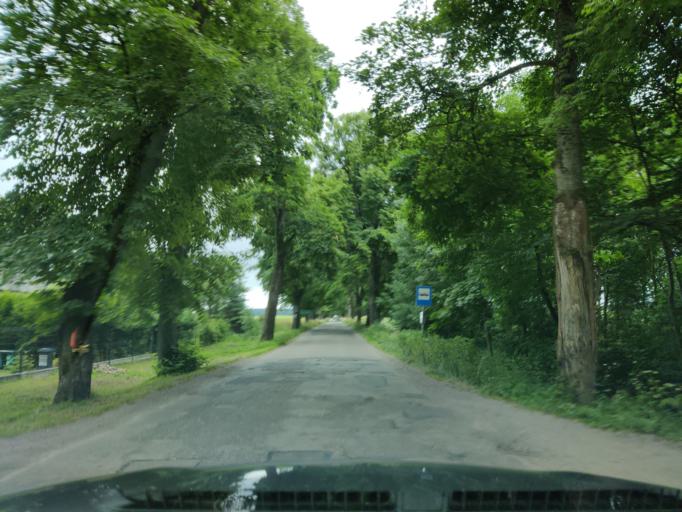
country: PL
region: Warmian-Masurian Voivodeship
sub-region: Powiat gizycki
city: Ryn
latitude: 53.9165
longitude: 21.5564
